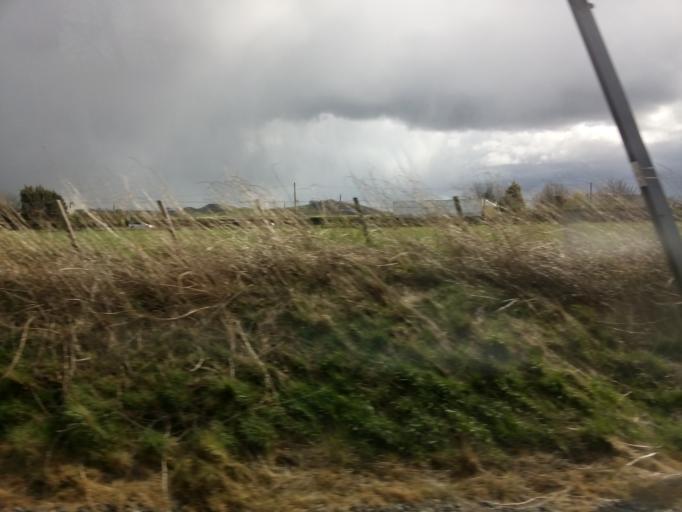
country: GB
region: Scotland
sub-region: East Lothian
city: Gullane
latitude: 55.9987
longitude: -2.8178
